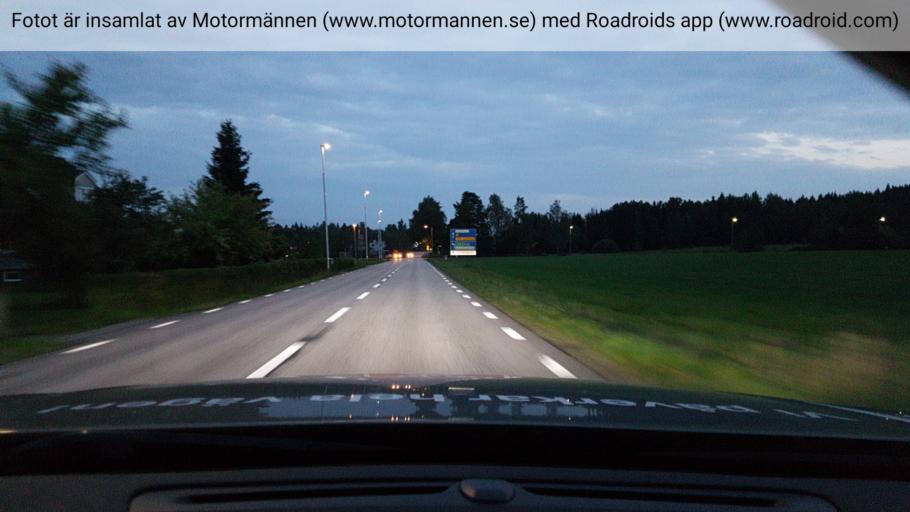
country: SE
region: OErebro
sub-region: Karlskoga Kommun
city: Karlskoga
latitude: 59.3513
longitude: 14.5710
